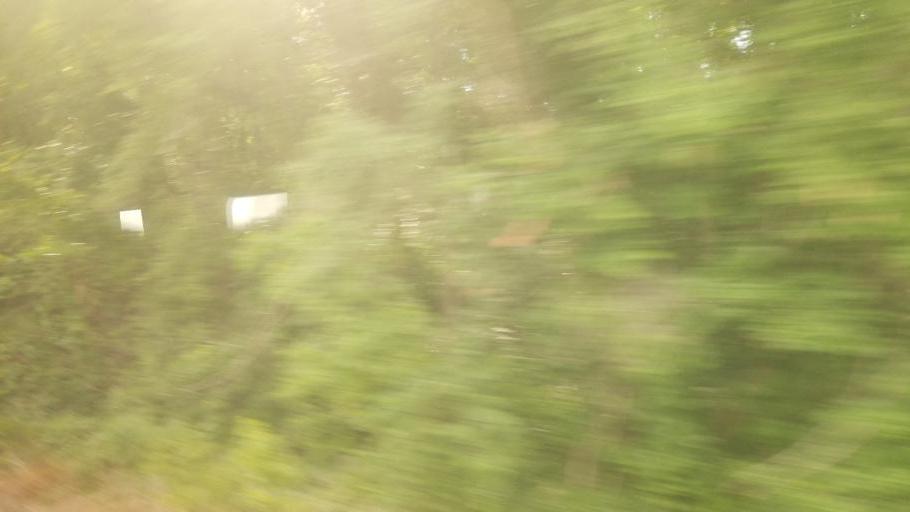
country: US
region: Kansas
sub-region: Douglas County
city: Eudora
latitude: 38.9574
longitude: -95.0768
